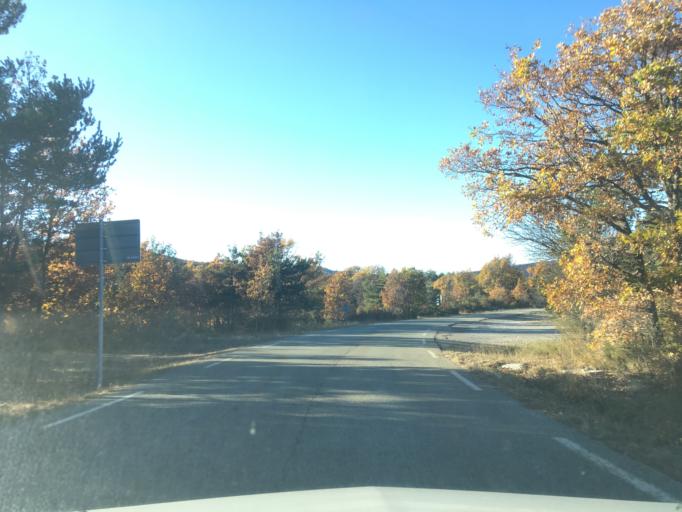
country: FR
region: Provence-Alpes-Cote d'Azur
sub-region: Departement du Var
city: Montferrat
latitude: 43.7365
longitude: 6.4330
